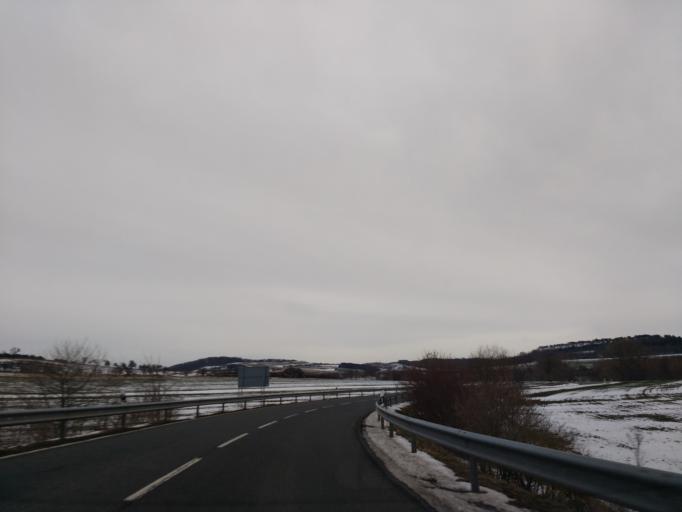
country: DE
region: Lower Saxony
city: Gemeinde Friedland
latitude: 51.3993
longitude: 9.9428
